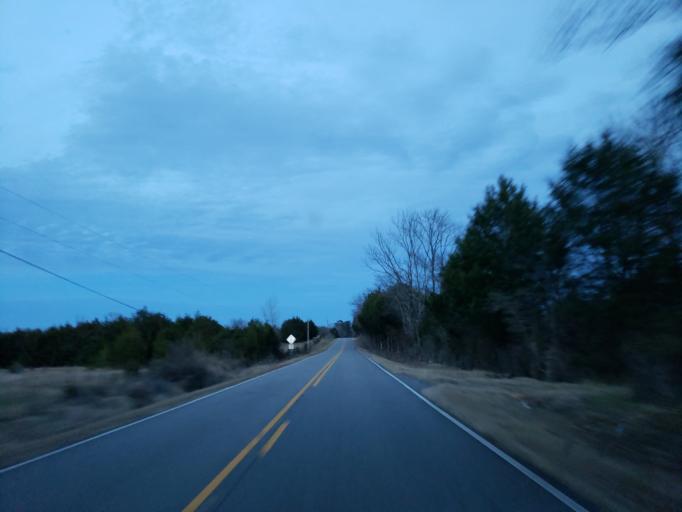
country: US
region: Alabama
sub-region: Greene County
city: Eutaw
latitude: 32.8786
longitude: -88.0750
